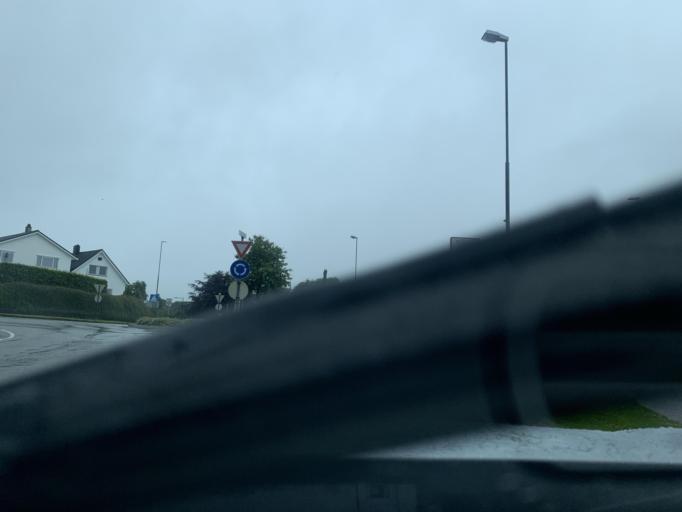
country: NO
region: Rogaland
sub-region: Time
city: Bryne
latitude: 58.7309
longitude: 5.6481
